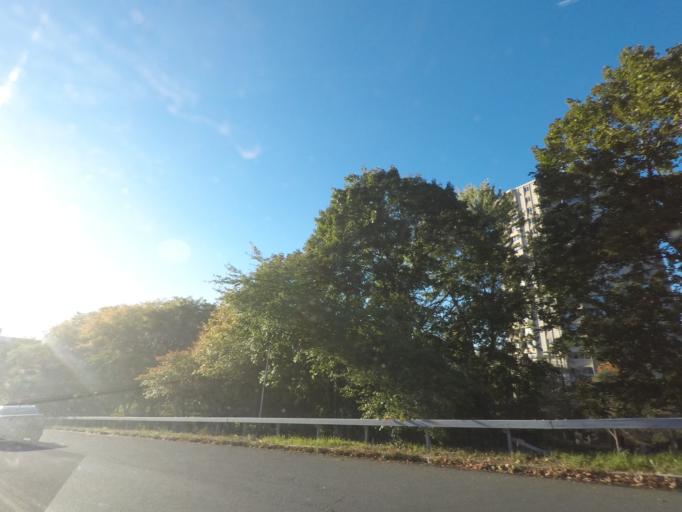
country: US
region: New York
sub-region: Rensselaer County
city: Troy
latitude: 42.7337
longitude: -73.6834
